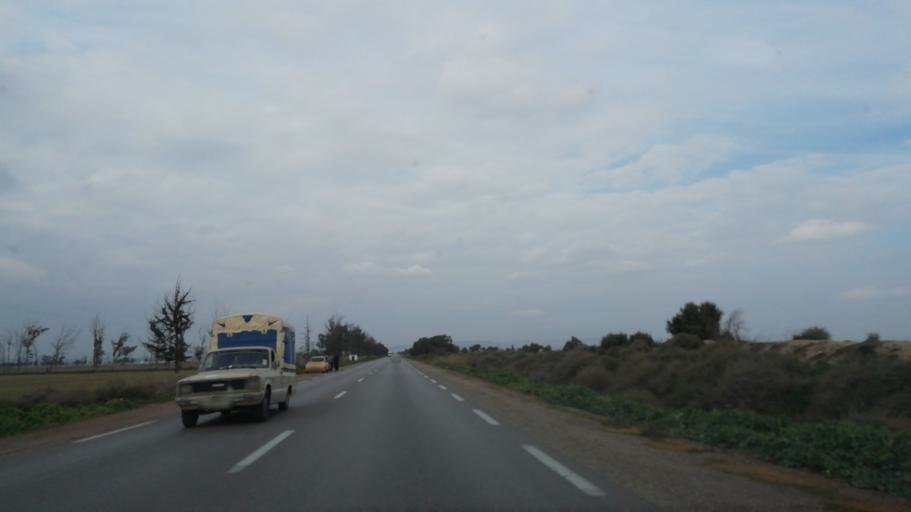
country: DZ
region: Mostaganem
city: Mostaganem
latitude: 35.6743
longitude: 0.0575
